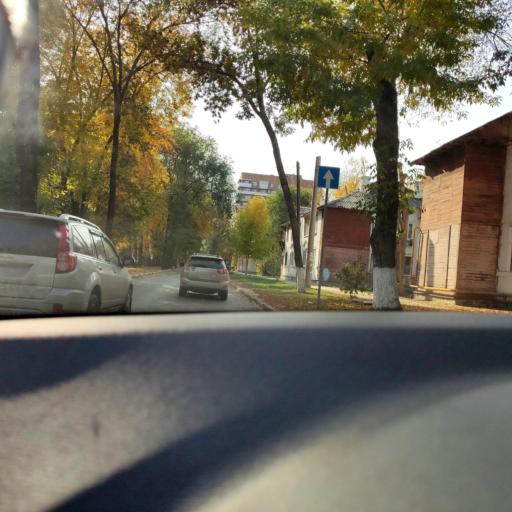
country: RU
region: Samara
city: Samara
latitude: 53.2329
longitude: 50.2626
